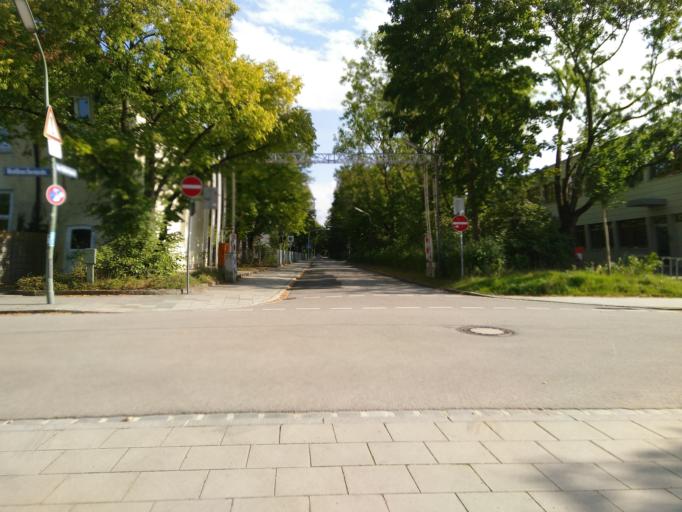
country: DE
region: Bavaria
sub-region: Upper Bavaria
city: Munich
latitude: 48.0978
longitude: 11.5736
